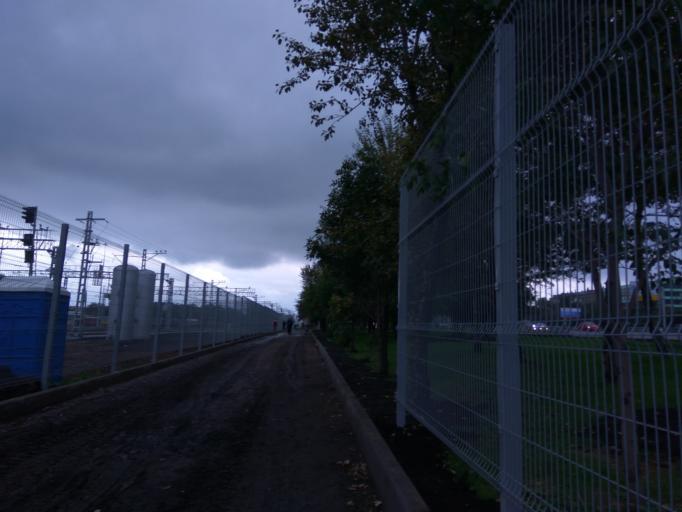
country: RU
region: Moscow
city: Taganskiy
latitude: 55.7177
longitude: 37.6940
